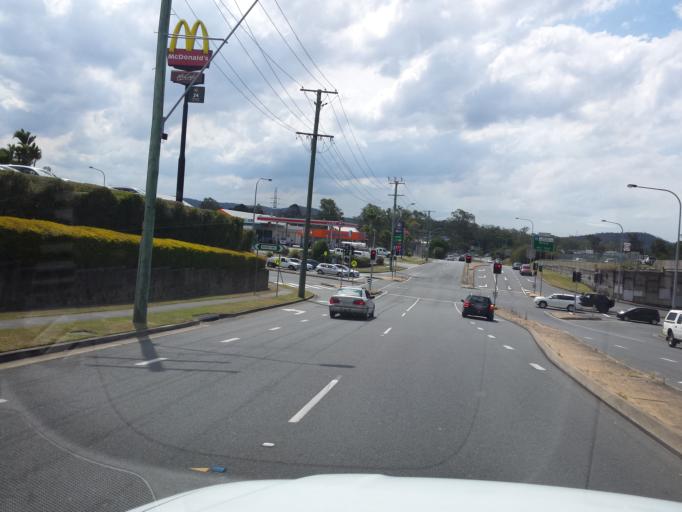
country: AU
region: Queensland
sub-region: Gold Coast
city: Nerang
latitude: -28.0079
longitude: 153.3426
